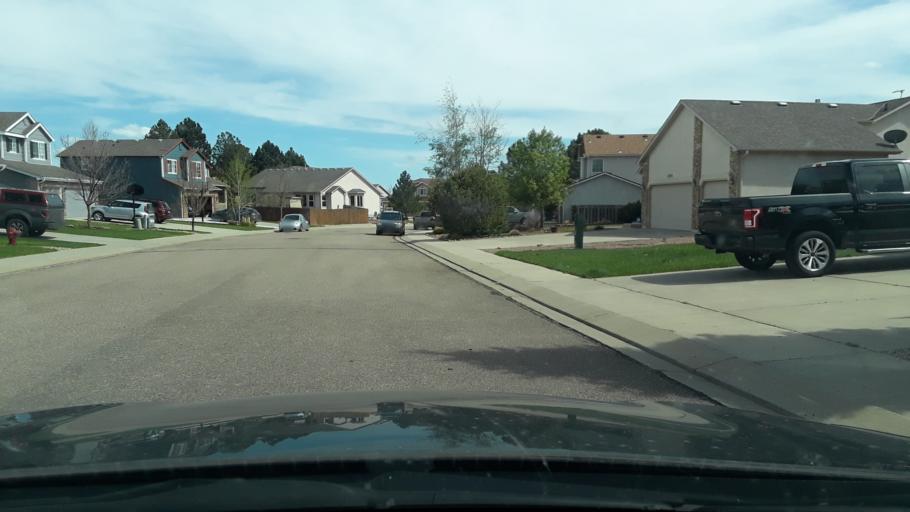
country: US
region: Colorado
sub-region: El Paso County
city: Monument
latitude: 39.0763
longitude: -104.8676
